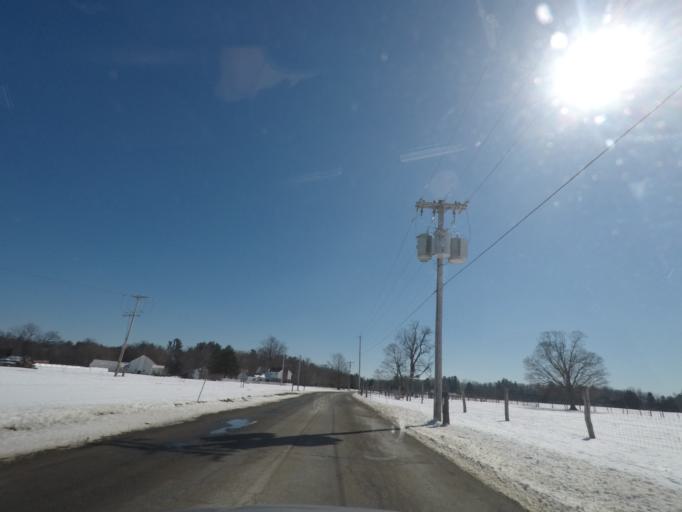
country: US
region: New York
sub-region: Saratoga County
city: Stillwater
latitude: 42.9110
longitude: -73.6083
